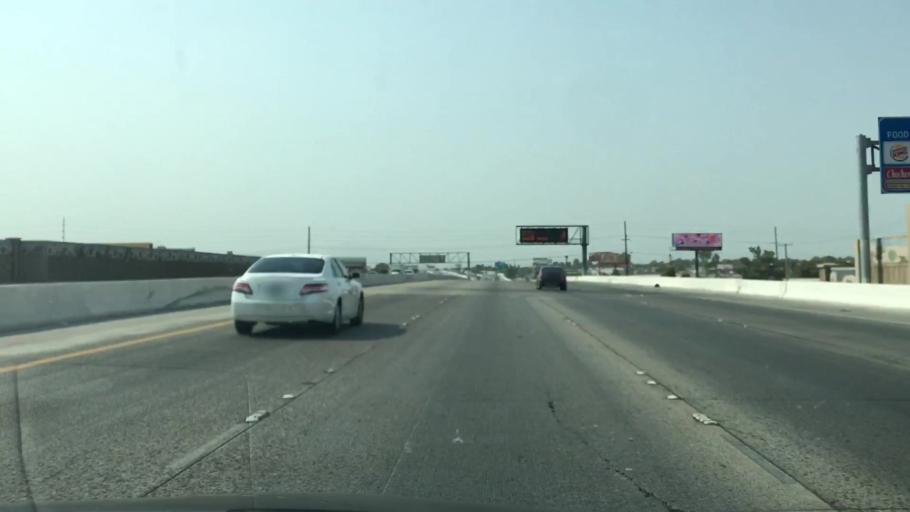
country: US
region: Nevada
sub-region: Clark County
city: Winchester
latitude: 36.1465
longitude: -115.0918
